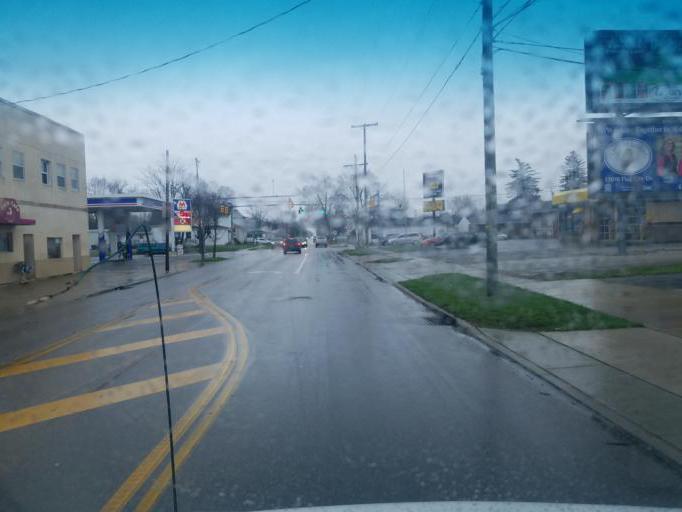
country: US
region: Ohio
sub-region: Hancock County
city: Findlay
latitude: 41.0369
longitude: -83.6421
